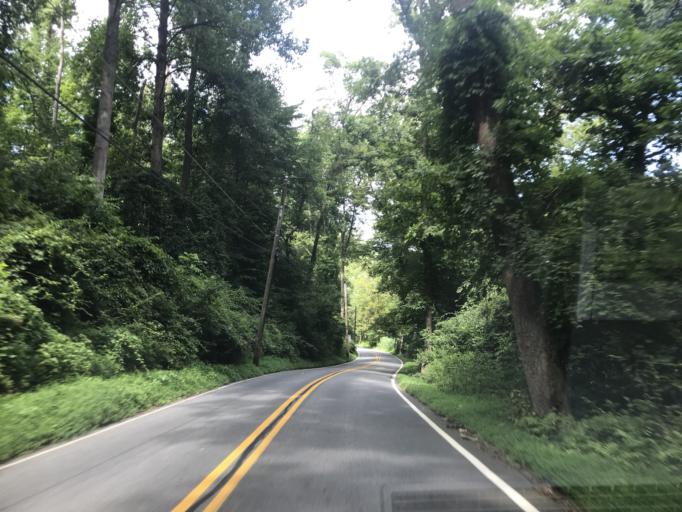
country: US
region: Delaware
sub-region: New Castle County
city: Greenville
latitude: 39.8444
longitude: -75.5694
